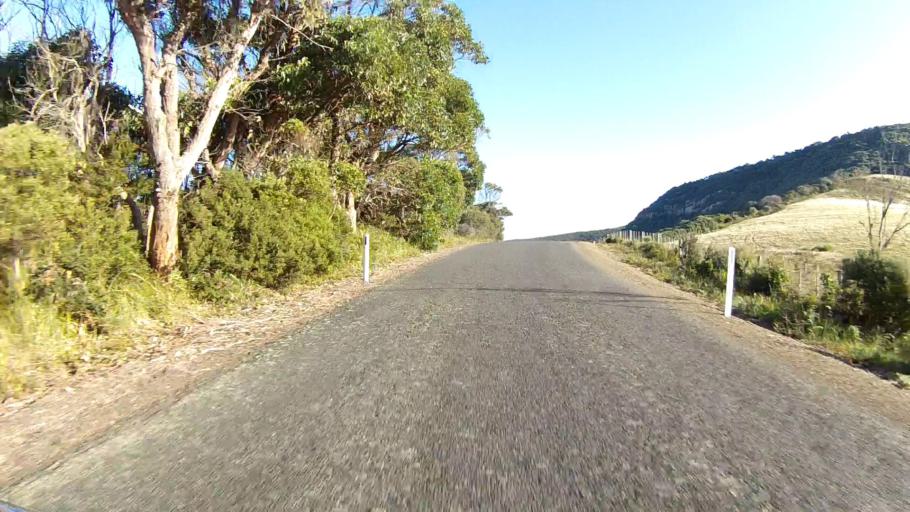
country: AU
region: Tasmania
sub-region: Clarence
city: Sandford
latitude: -43.1856
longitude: 147.8481
